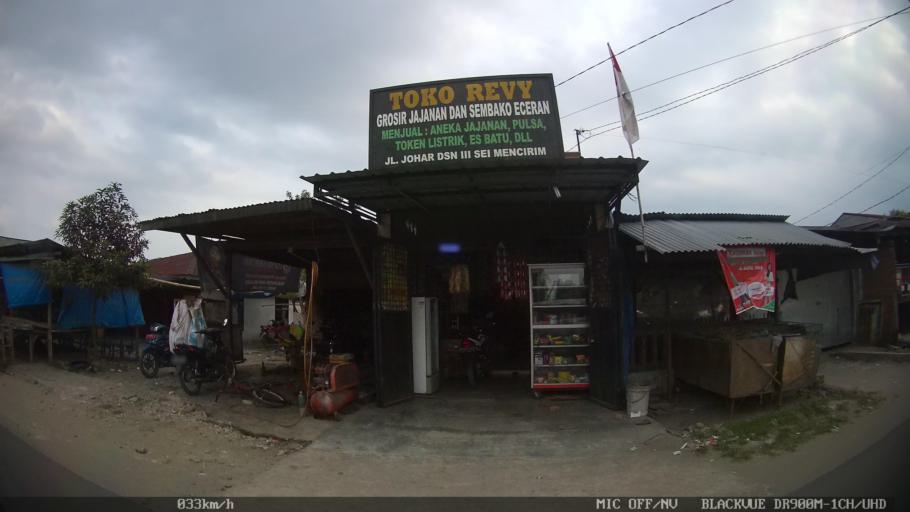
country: ID
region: North Sumatra
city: Sunggal
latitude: 3.5582
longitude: 98.5533
